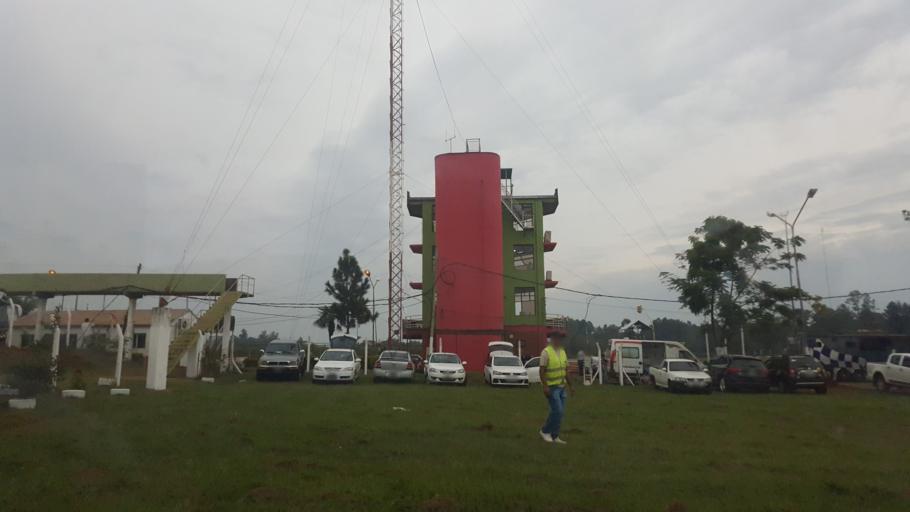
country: AR
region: Entre Rios
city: Concepcion del Uruguay
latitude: -32.4544
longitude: -58.3181
